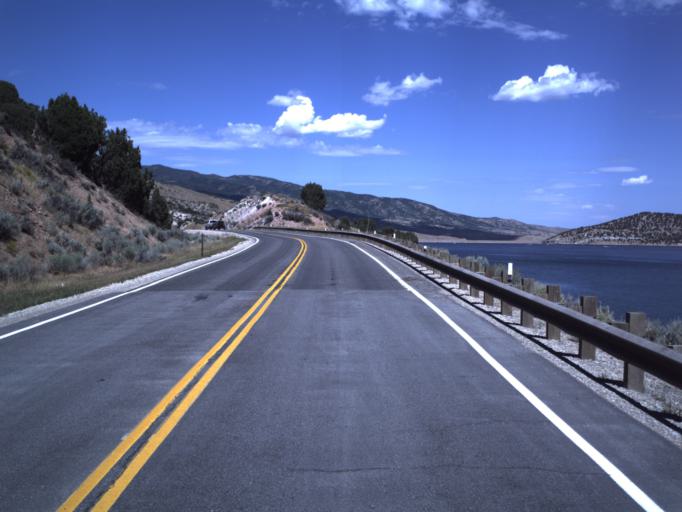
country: US
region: Utah
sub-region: Summit County
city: Oakley
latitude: 40.7647
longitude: -111.3982
